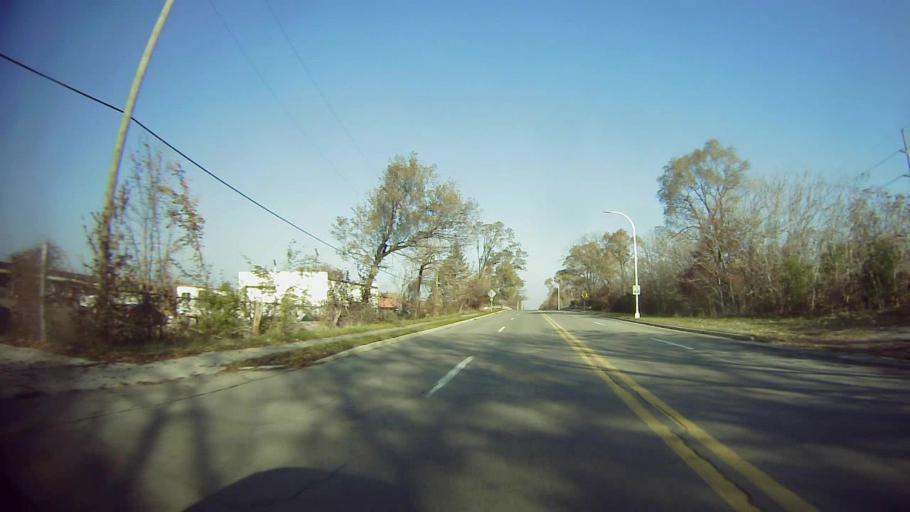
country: US
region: Michigan
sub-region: Wayne County
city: Dearborn
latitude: 42.3293
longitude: -83.1664
